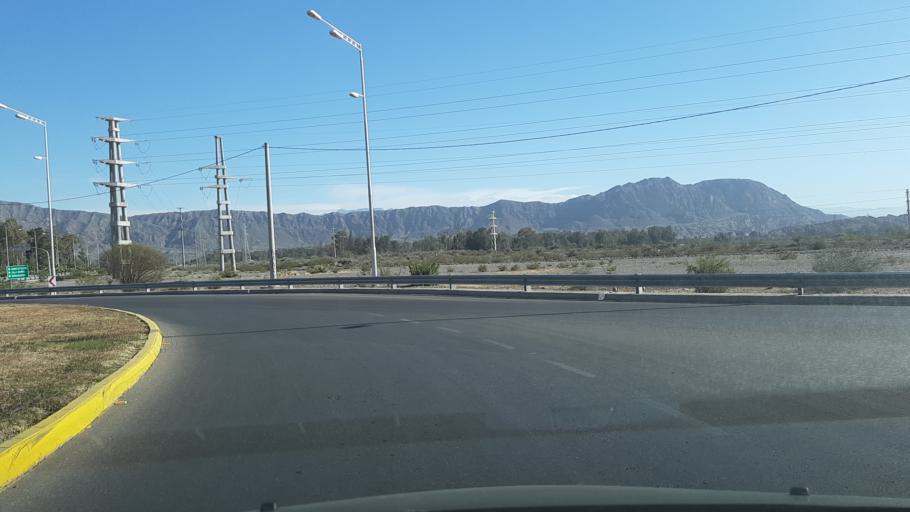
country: AR
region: San Juan
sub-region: Departamento de Rivadavia
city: Rivadavia
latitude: -31.5154
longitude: -68.6306
